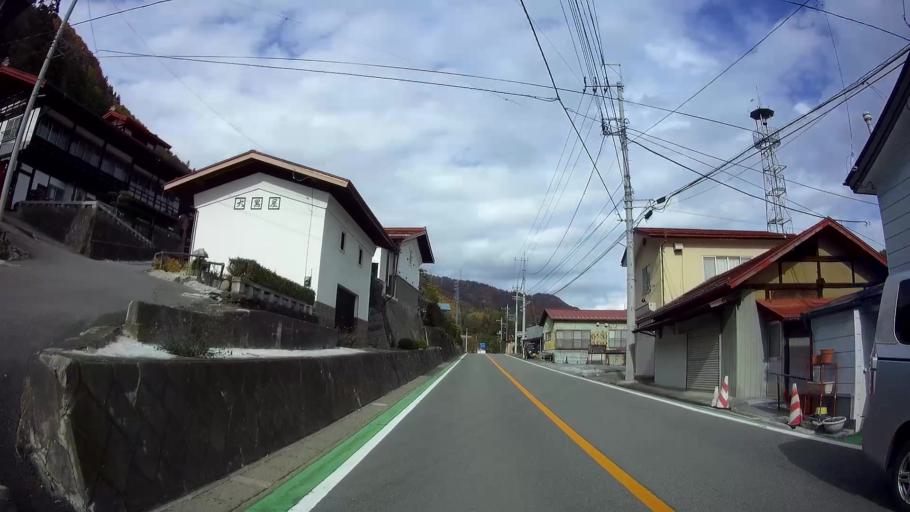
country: JP
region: Gunma
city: Nakanojomachi
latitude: 36.5978
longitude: 138.6280
